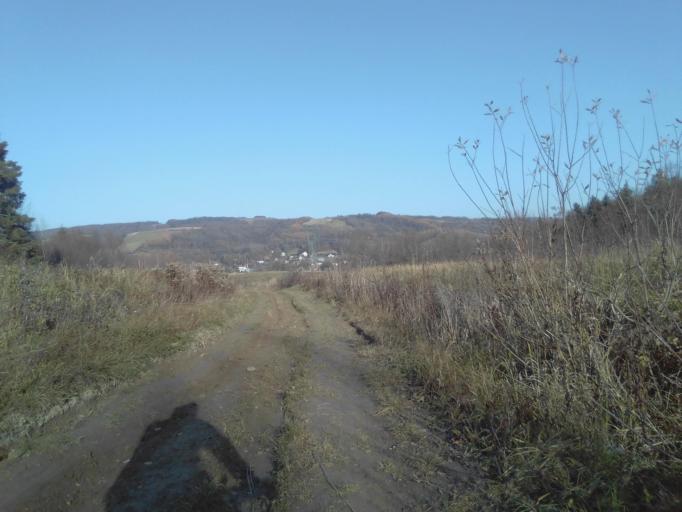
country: PL
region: Subcarpathian Voivodeship
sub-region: Powiat strzyzowski
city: Jawornik
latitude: 49.7963
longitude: 21.8849
